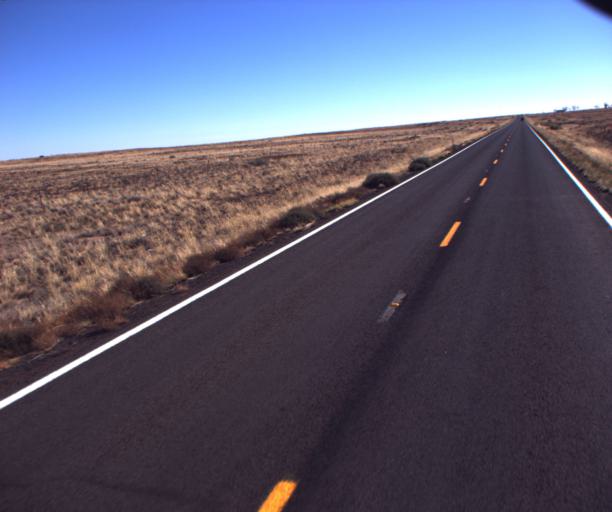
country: US
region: Arizona
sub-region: Coconino County
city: Tuba City
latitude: 35.9644
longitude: -110.9478
